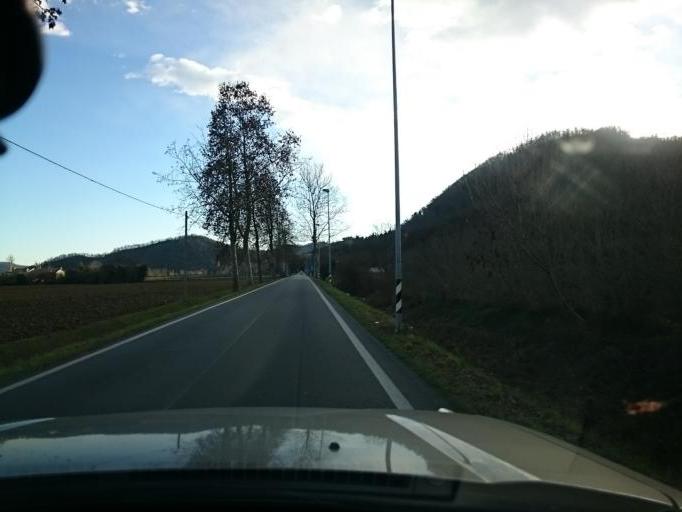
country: IT
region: Veneto
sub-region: Provincia di Padova
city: San Biagio
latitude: 45.3714
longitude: 11.7364
